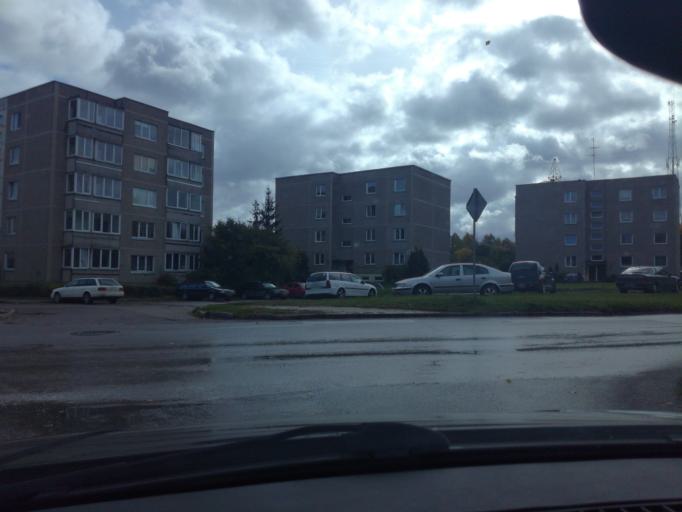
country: LT
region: Alytaus apskritis
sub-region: Alytus
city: Alytus
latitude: 54.3906
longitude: 24.0294
